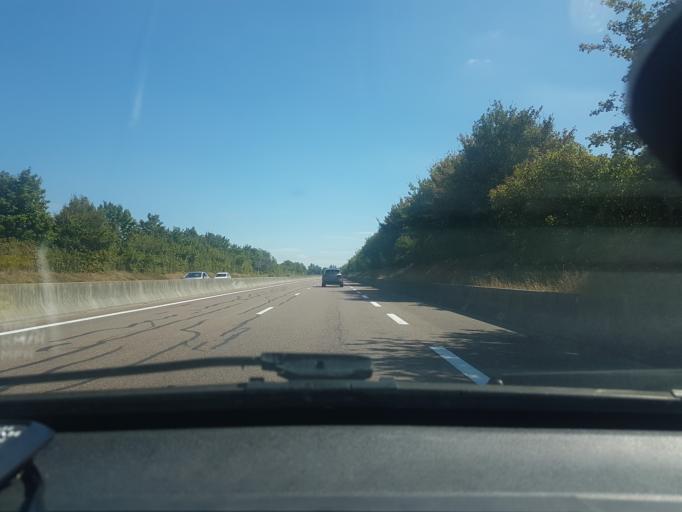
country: FR
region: Bourgogne
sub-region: Departement de la Cote-d'Or
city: Couternon
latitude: 47.3453
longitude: 5.1471
